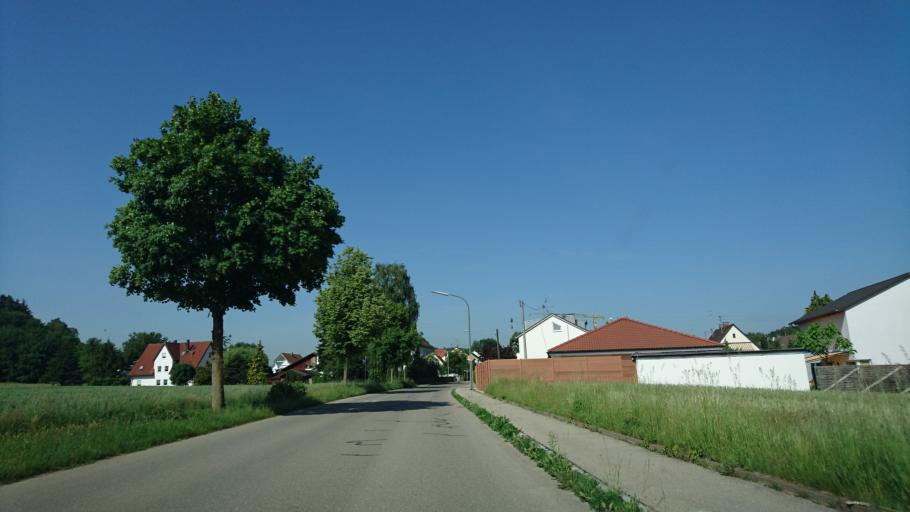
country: DE
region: Bavaria
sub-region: Swabia
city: Diedorf
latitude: 48.3570
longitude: 10.7509
